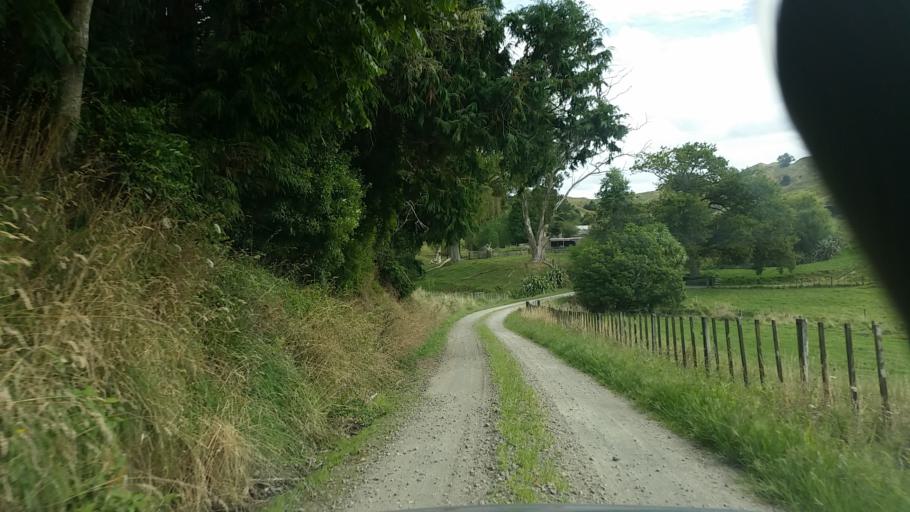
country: NZ
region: Taranaki
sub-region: South Taranaki District
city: Eltham
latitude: -39.2573
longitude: 174.5626
